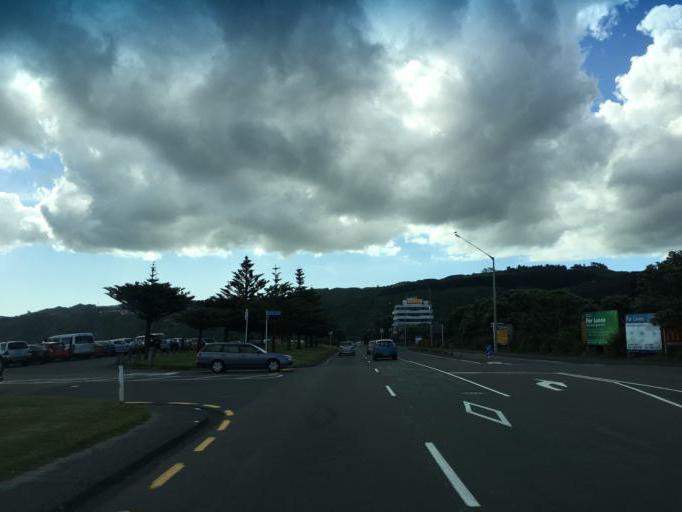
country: NZ
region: Wellington
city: Petone
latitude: -41.2271
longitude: 174.8728
